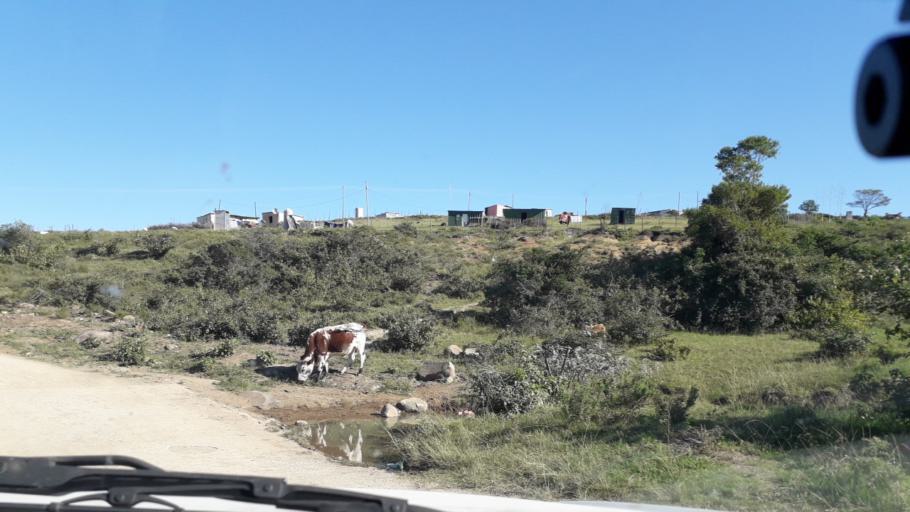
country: ZA
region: Eastern Cape
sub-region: Buffalo City Metropolitan Municipality
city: East London
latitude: -32.7991
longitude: 27.9667
